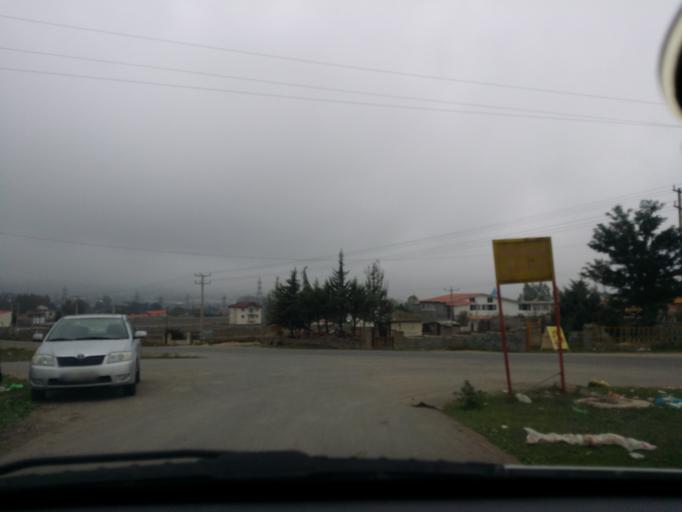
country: IR
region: Mazandaran
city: Chalus
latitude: 36.5140
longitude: 51.2263
